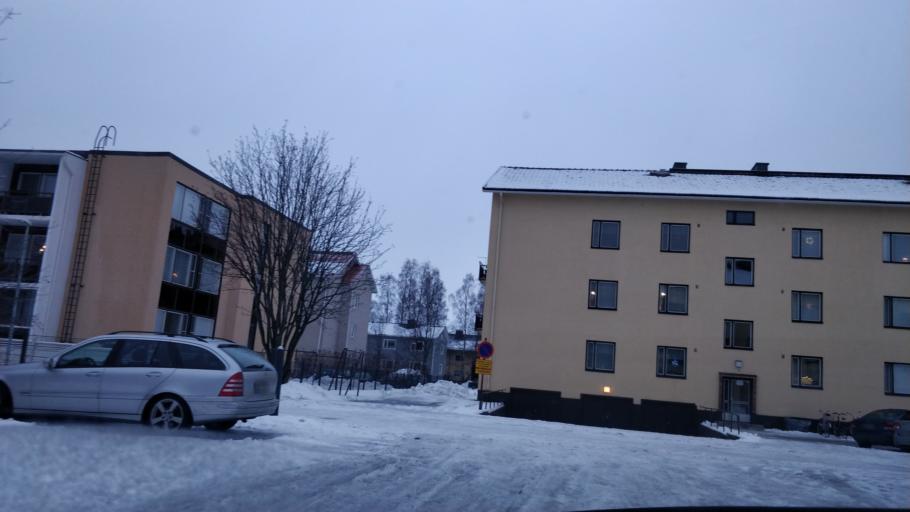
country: FI
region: Lapland
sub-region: Kemi-Tornio
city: Kemi
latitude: 65.7416
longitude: 24.5639
